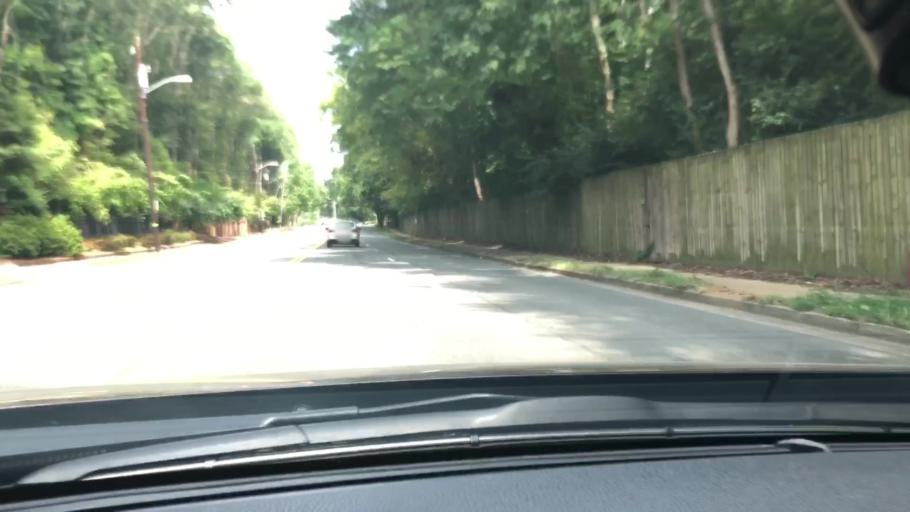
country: US
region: North Carolina
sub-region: Mecklenburg County
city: Charlotte
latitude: 35.1675
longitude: -80.8257
